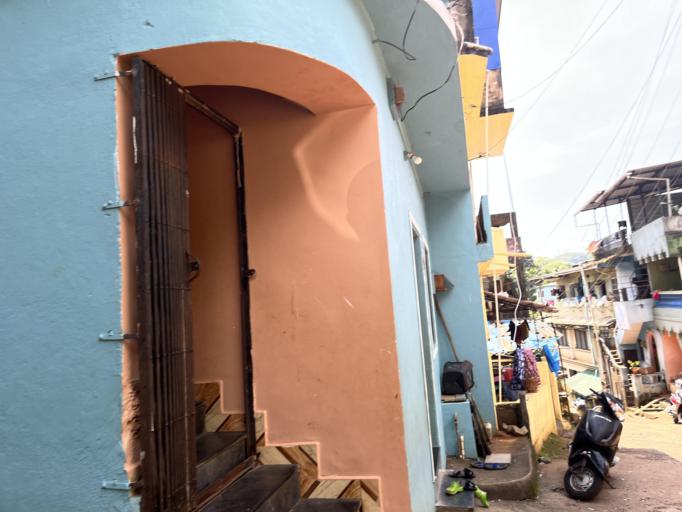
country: IN
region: Goa
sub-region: North Goa
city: Ponda
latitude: 15.4064
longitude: 74.0118
